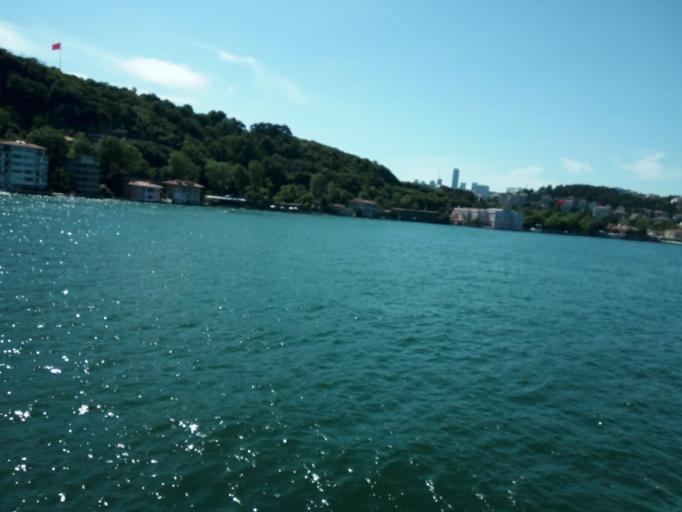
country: TR
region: Istanbul
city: Sisli
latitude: 41.0929
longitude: 29.0581
